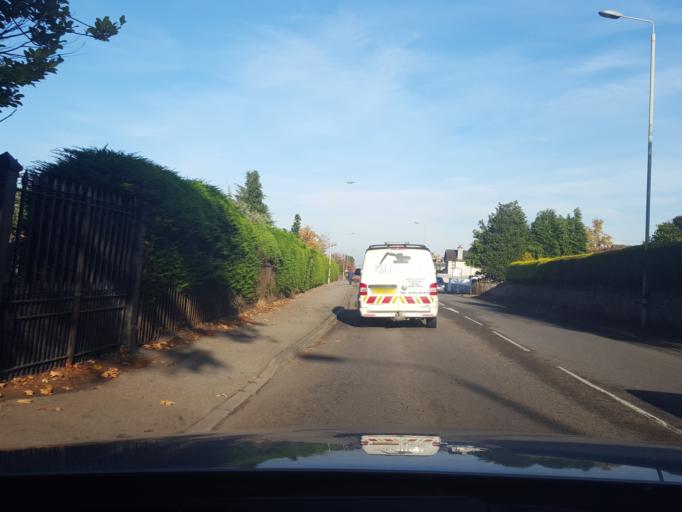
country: GB
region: Scotland
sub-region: Highland
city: Inverness
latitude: 57.4673
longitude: -4.2391
